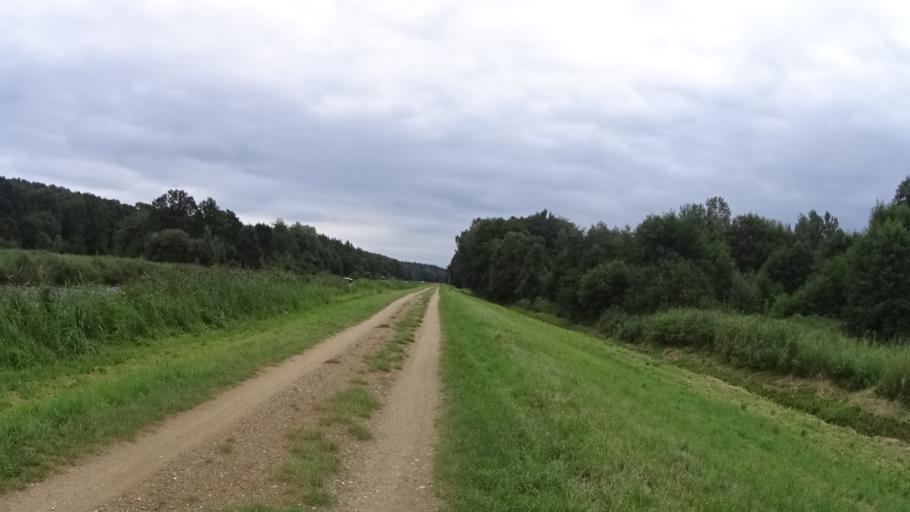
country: DE
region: Schleswig-Holstein
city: Panten
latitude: 53.6579
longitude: 10.6408
